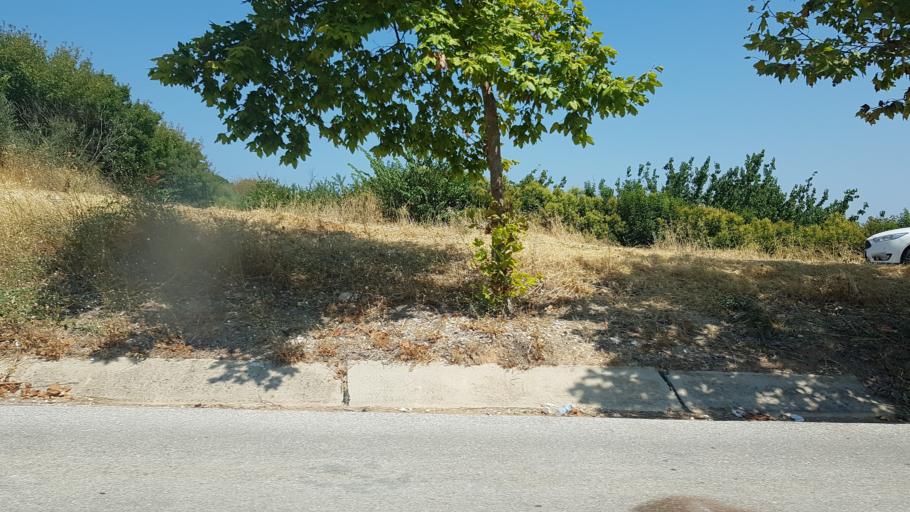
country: TR
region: Izmir
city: Urla
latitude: 38.3262
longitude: 26.7785
